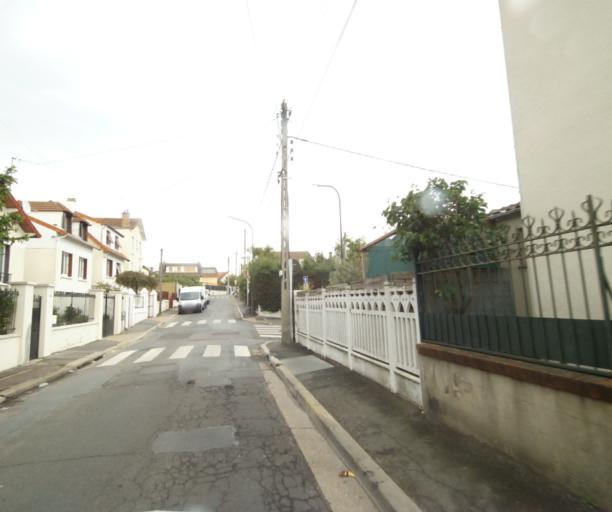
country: FR
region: Ile-de-France
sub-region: Departement du Val-d'Oise
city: Bezons
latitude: 48.9443
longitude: 2.2252
